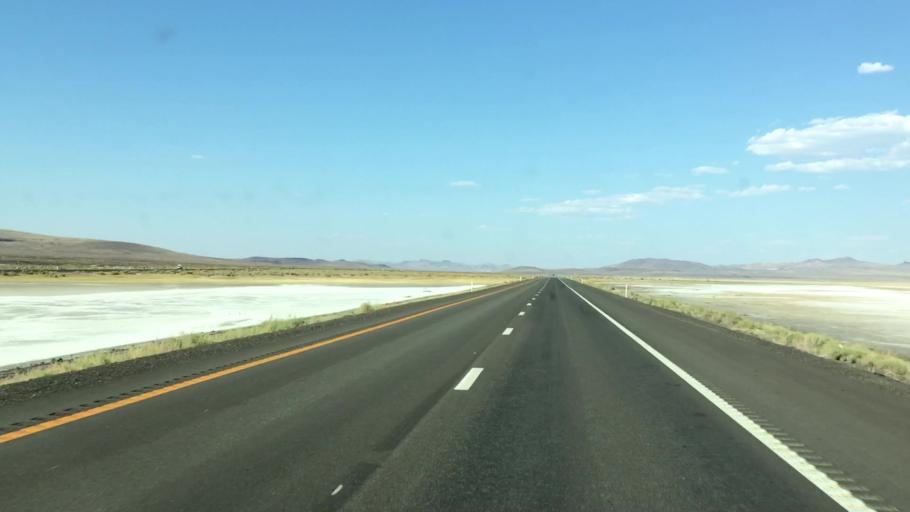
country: US
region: Nevada
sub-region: Lyon County
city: Fernley
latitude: 39.7068
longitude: -119.0946
